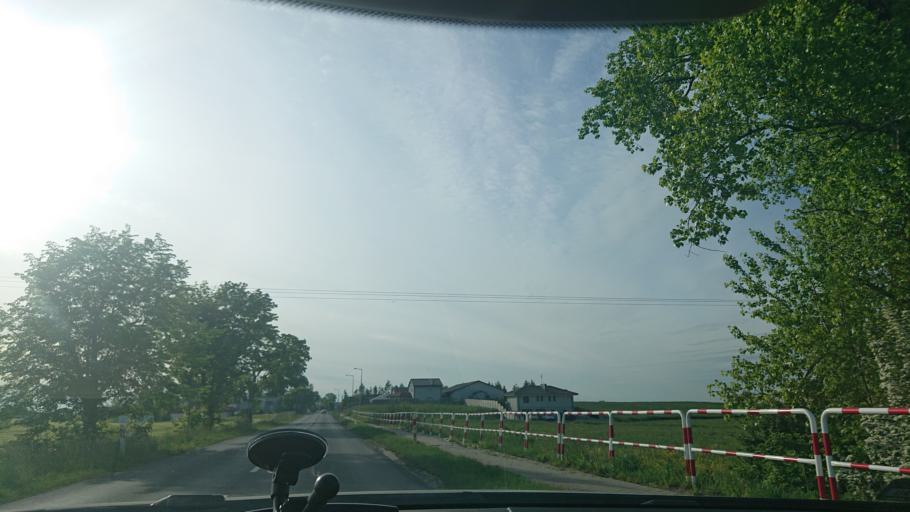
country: PL
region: Greater Poland Voivodeship
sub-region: Powiat gnieznienski
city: Gniezno
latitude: 52.5468
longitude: 17.5623
